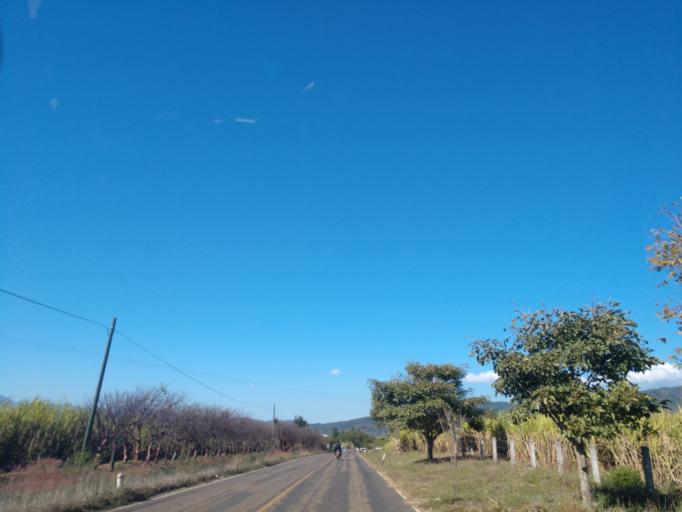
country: MX
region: Nayarit
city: Compostela
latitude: 21.2670
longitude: -104.8923
